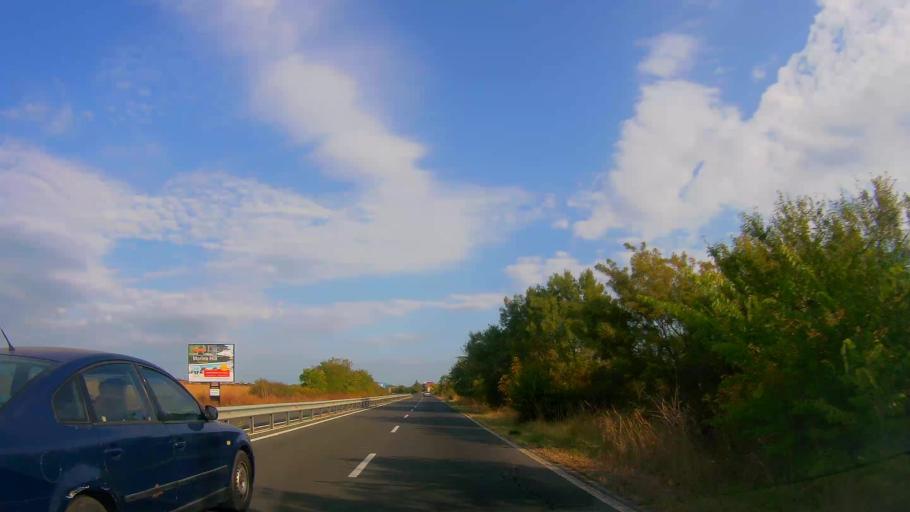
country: BG
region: Burgas
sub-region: Obshtina Sozopol
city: Chernomorets
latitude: 42.4281
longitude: 27.6402
